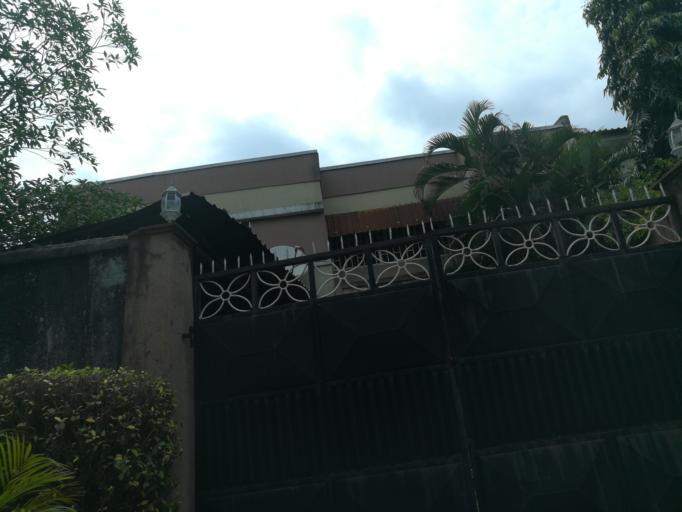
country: NG
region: Lagos
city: Ojota
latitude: 6.5775
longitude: 3.3699
